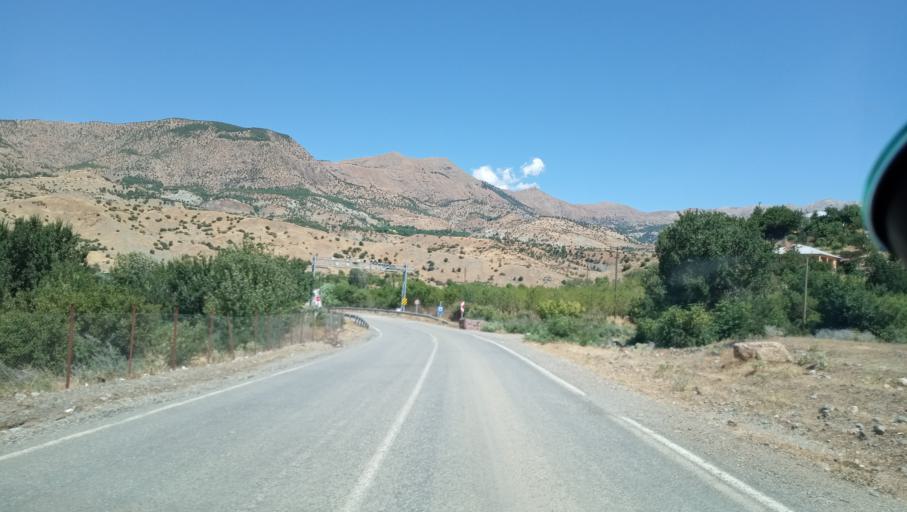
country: TR
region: Diyarbakir
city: Kulp
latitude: 38.5007
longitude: 41.0449
